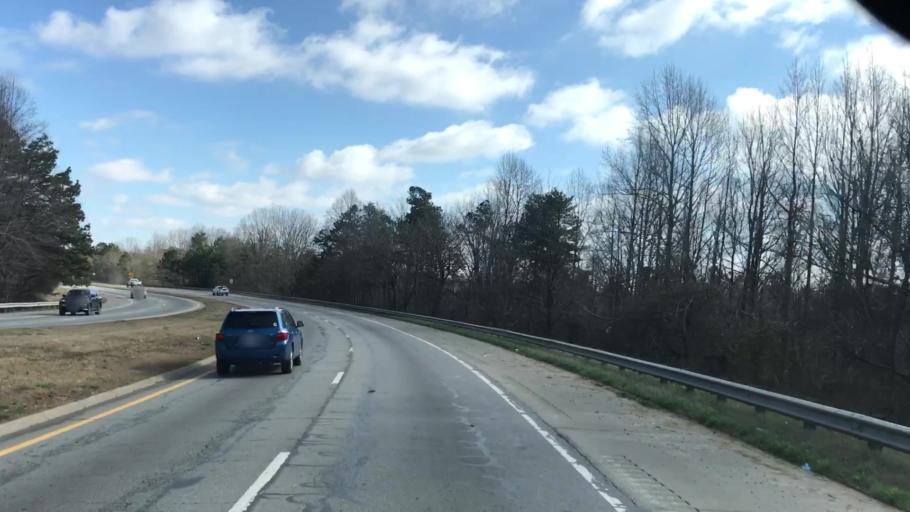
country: US
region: Georgia
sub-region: Hall County
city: Gainesville
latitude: 34.2818
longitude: -83.7982
